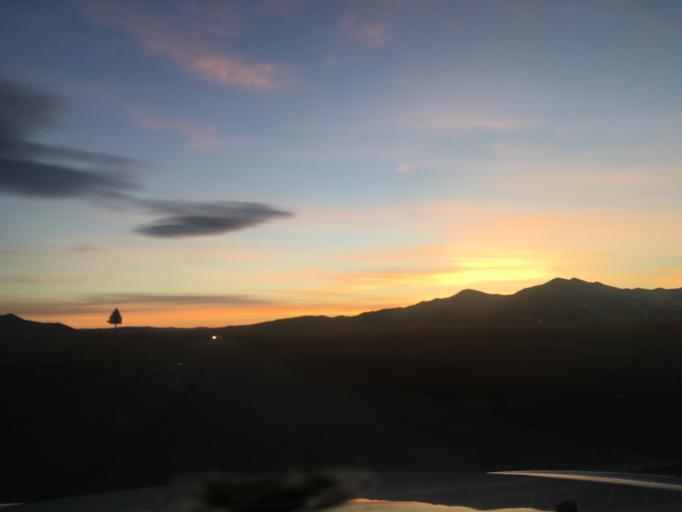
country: MN
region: Central Aimak
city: Mandal
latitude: 48.1007
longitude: 106.6198
